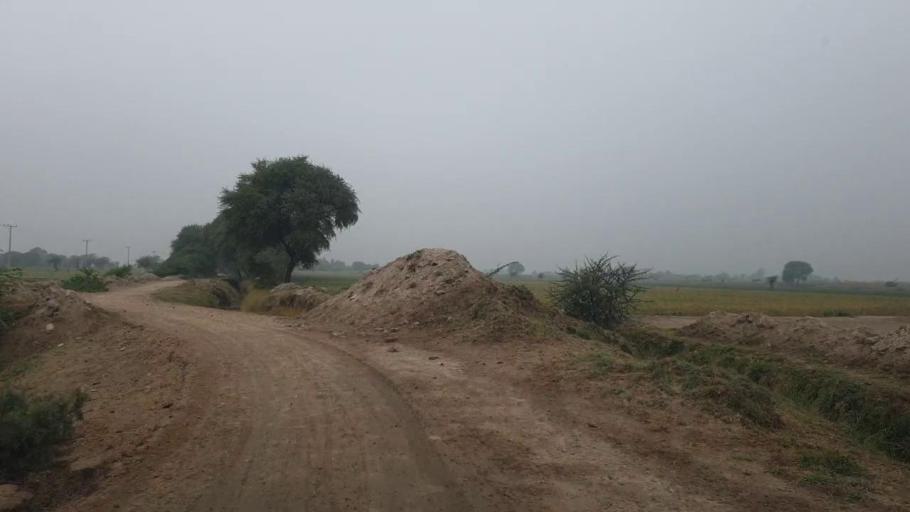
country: PK
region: Sindh
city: Badin
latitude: 24.6324
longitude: 68.6861
